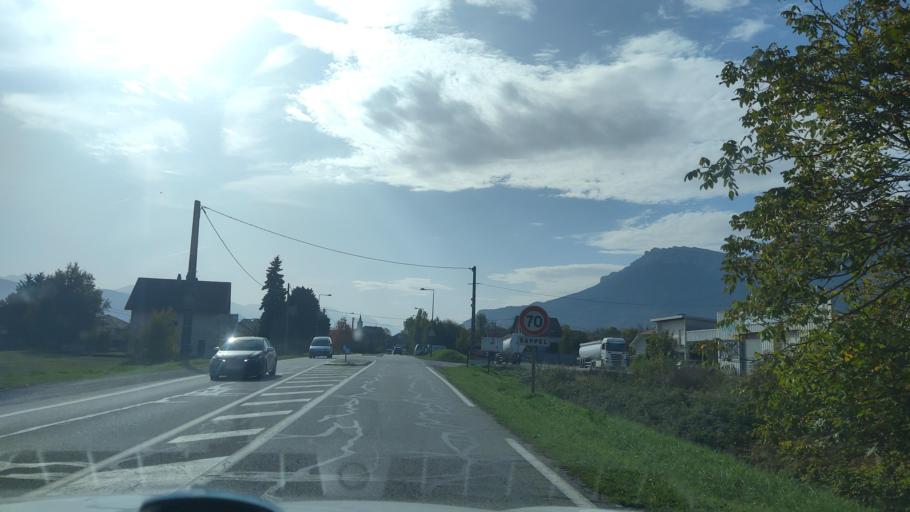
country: FR
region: Rhone-Alpes
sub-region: Departement de la Savoie
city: Les Marches
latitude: 45.5063
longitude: 6.0028
